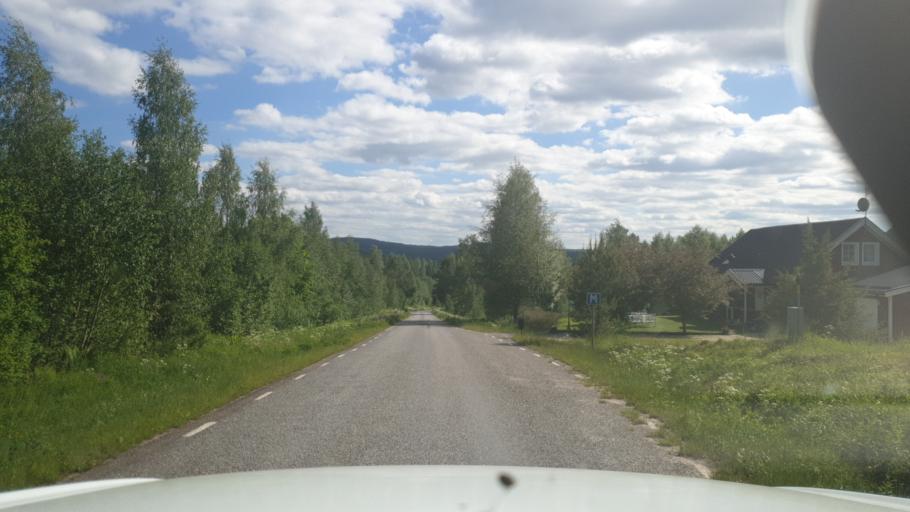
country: SE
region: Vaermland
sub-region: Eda Kommun
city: Charlottenberg
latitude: 59.9778
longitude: 12.4119
